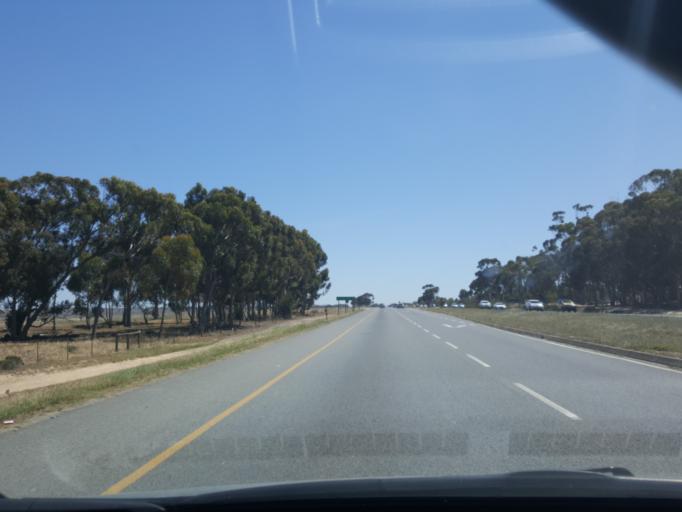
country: ZA
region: Western Cape
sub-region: City of Cape Town
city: Sunset Beach
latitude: -33.7706
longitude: 18.5479
